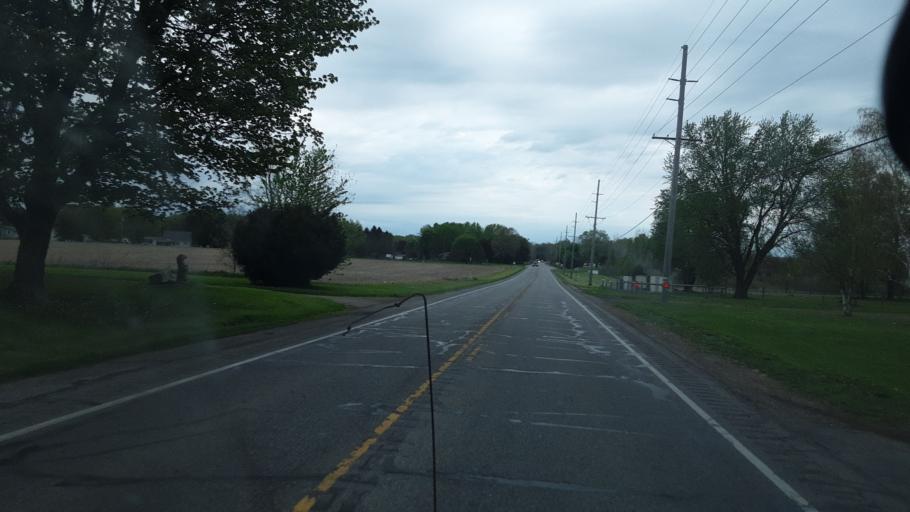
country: US
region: Indiana
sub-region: Elkhart County
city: Goshen
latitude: 41.6317
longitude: -85.8292
